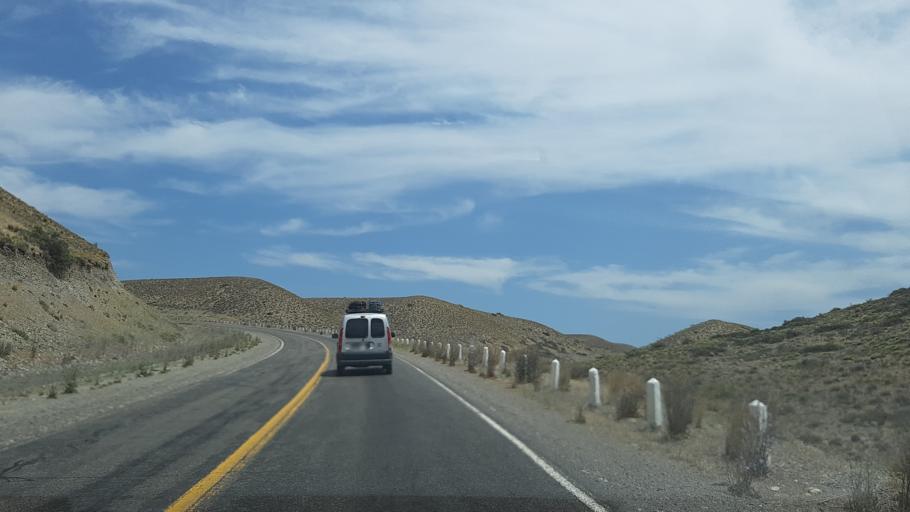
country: AR
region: Rio Negro
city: Pilcaniyeu
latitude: -40.4834
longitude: -70.6775
